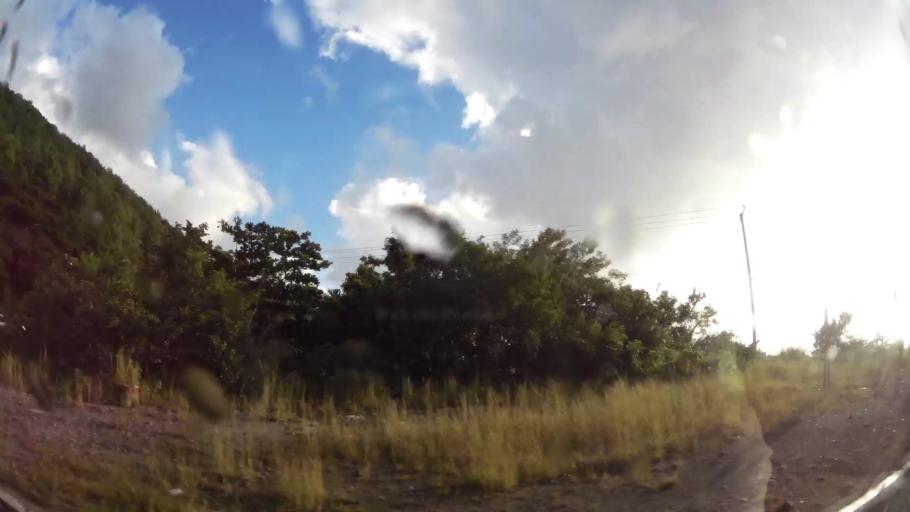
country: DM
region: Saint Joseph
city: Saint Joseph
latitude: 15.3859
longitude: -61.4128
